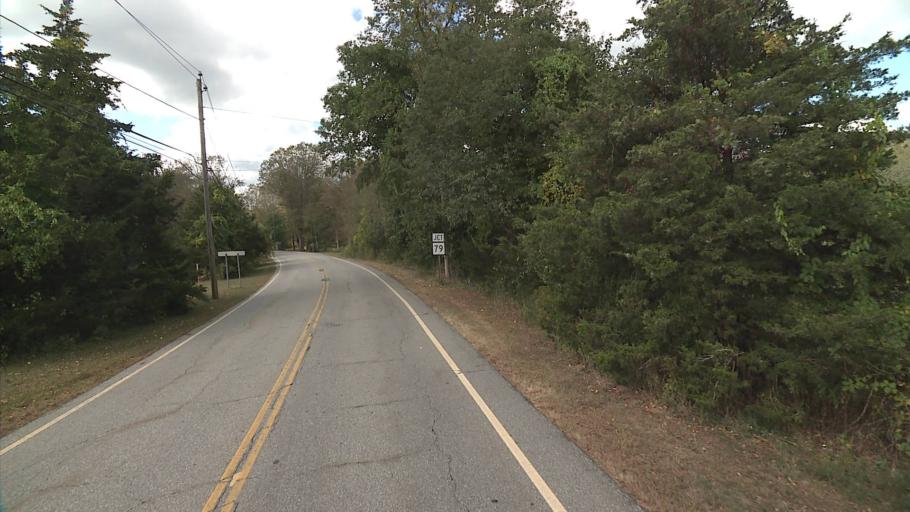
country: US
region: Connecticut
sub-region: Middlesex County
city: Durham
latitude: 41.4367
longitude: -72.6485
